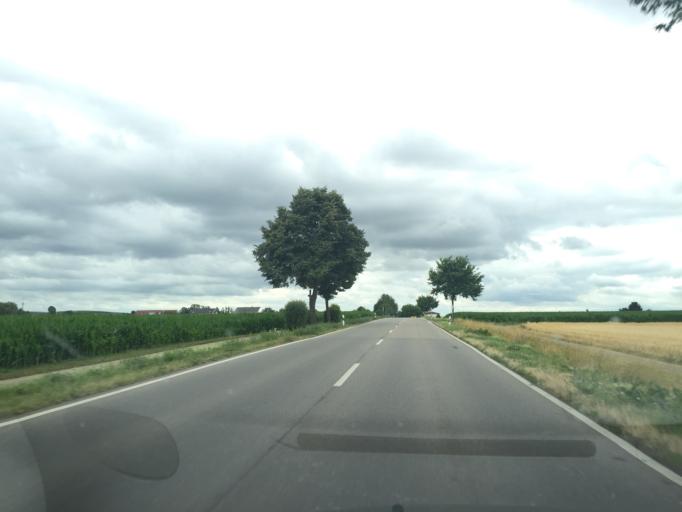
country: DE
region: Baden-Wuerttemberg
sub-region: Freiburg Region
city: Heitersheim
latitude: 47.8807
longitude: 7.6612
